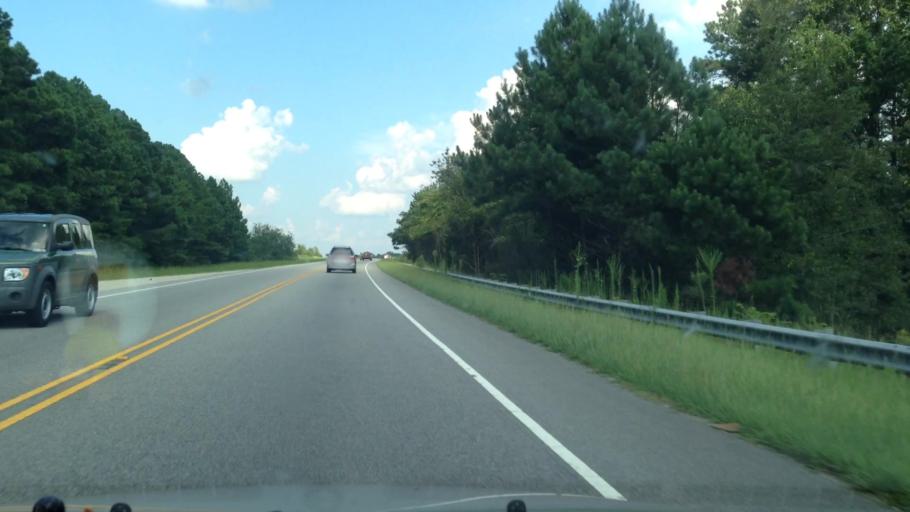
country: US
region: North Carolina
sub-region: Lee County
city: Broadway
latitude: 35.4391
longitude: -79.0461
